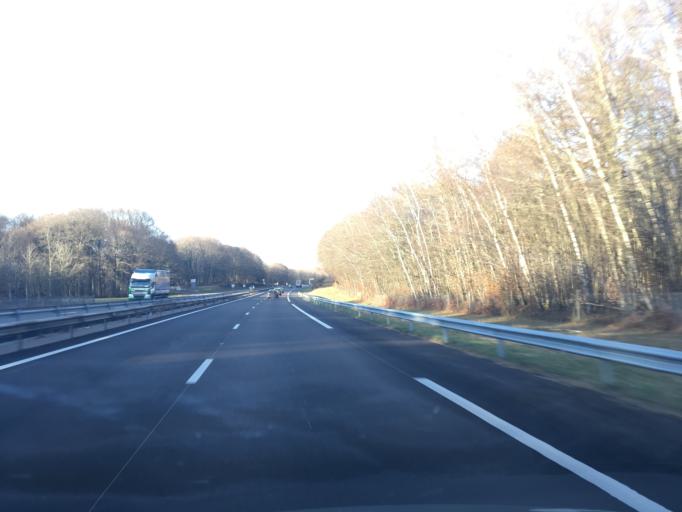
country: FR
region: Bourgogne
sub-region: Departement de l'Yonne
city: Joux-la-Ville
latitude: 47.5943
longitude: 3.9133
